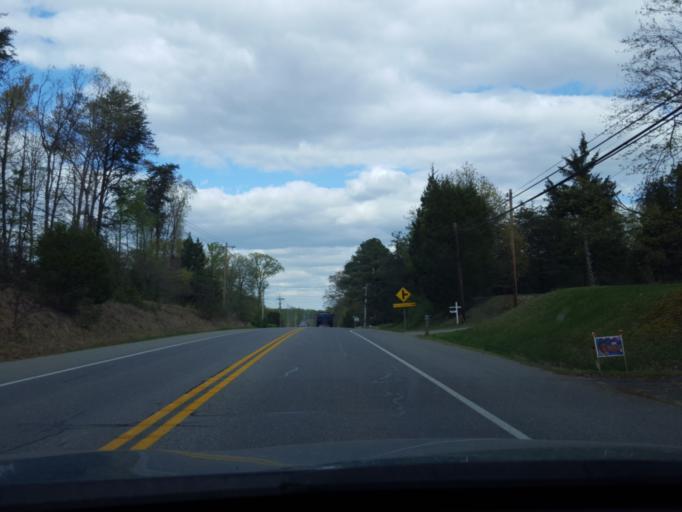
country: US
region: Maryland
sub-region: Charles County
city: La Plata
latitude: 38.5404
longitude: -76.9397
